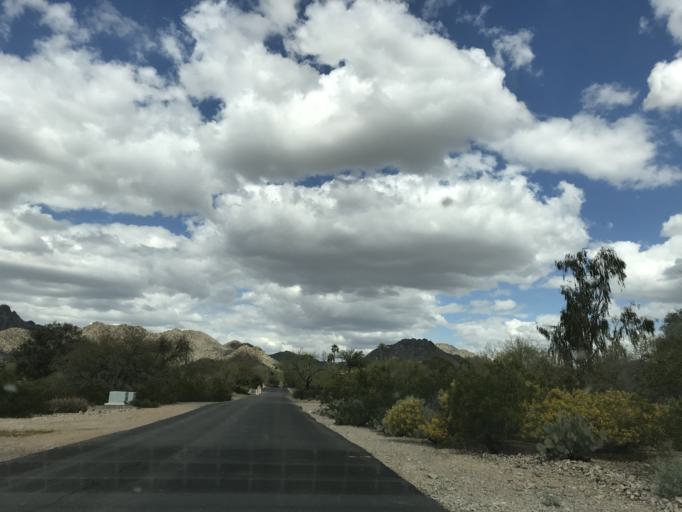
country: US
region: Arizona
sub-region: Maricopa County
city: Paradise Valley
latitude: 33.5202
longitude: -112.0066
